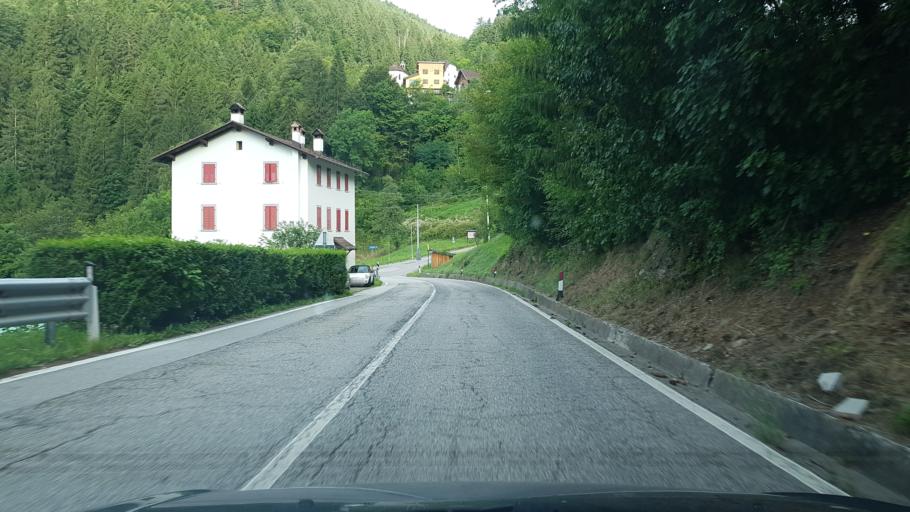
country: IT
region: Friuli Venezia Giulia
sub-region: Provincia di Udine
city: Comeglians
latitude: 46.5377
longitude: 12.8647
